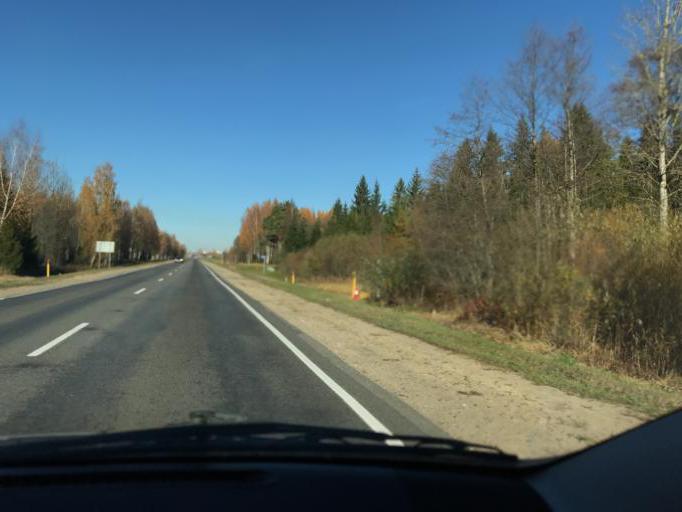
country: BY
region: Vitebsk
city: Polatsk
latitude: 55.4448
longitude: 28.7734
